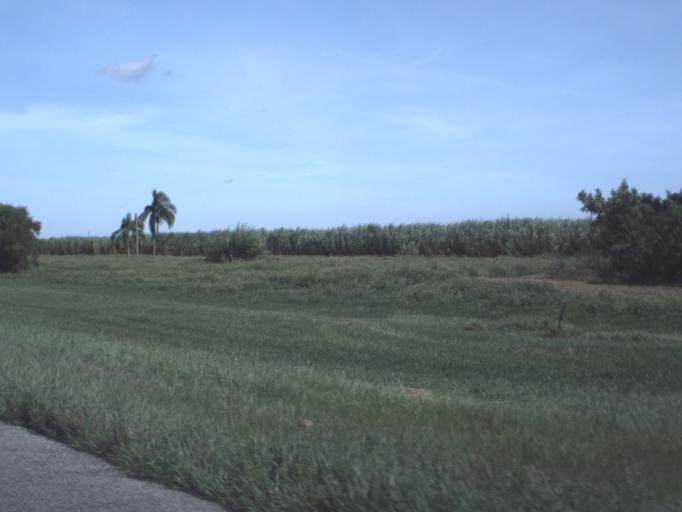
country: US
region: Florida
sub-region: Glades County
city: Moore Haven
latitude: 26.8065
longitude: -81.0824
